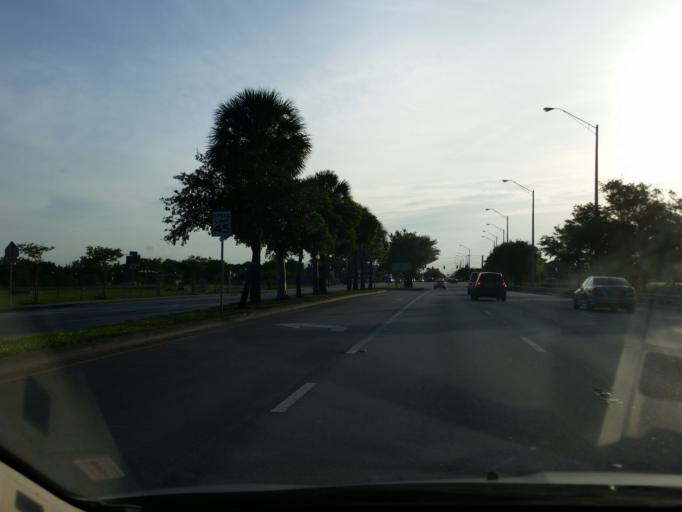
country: US
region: Florida
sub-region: Broward County
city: Davie
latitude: 26.0652
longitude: -80.2292
